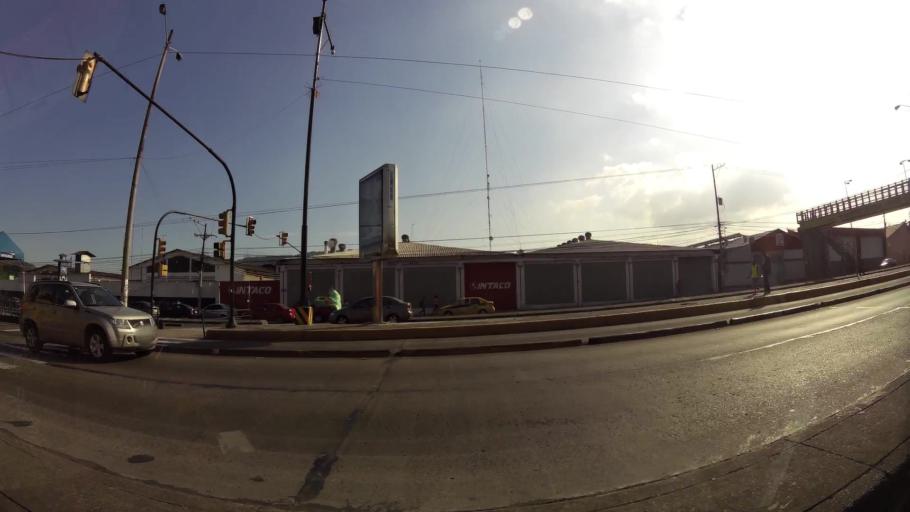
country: EC
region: Guayas
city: Guayaquil
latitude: -2.1526
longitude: -79.9313
